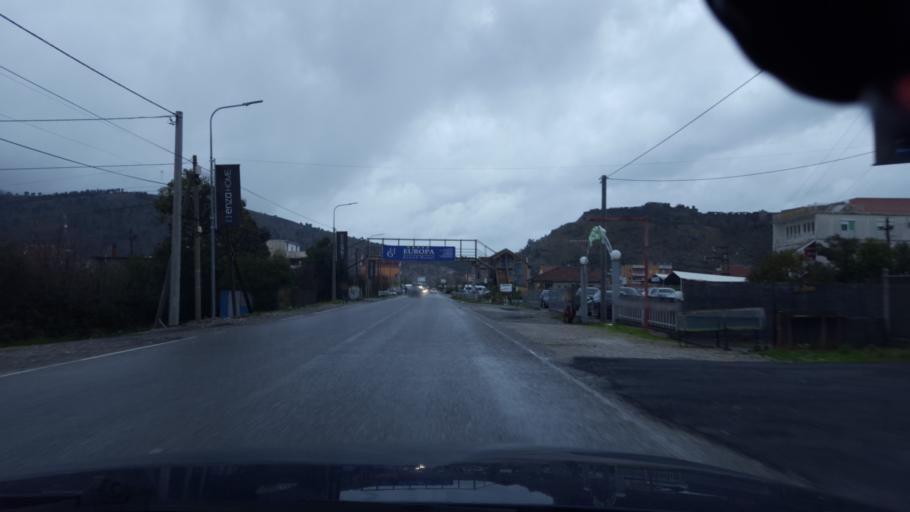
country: AL
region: Shkoder
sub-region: Rrethi i Shkodres
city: Berdica e Madhe
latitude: 42.0382
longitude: 19.4974
